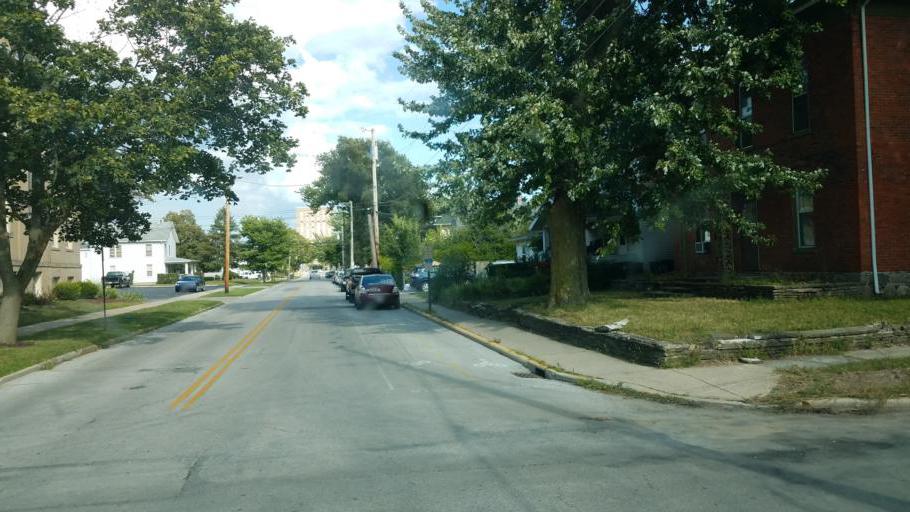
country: US
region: Ohio
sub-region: Wood County
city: Bowling Green
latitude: 41.3759
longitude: -83.6475
